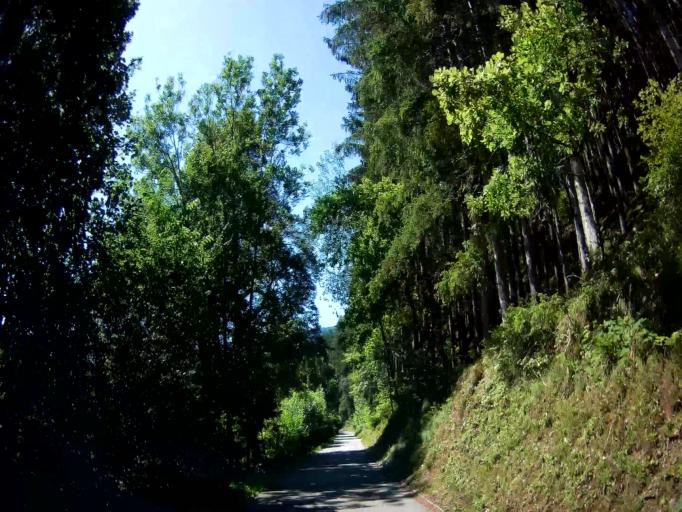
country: AT
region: Carinthia
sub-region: Politischer Bezirk Spittal an der Drau
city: Lendorf
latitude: 46.8240
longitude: 13.4427
